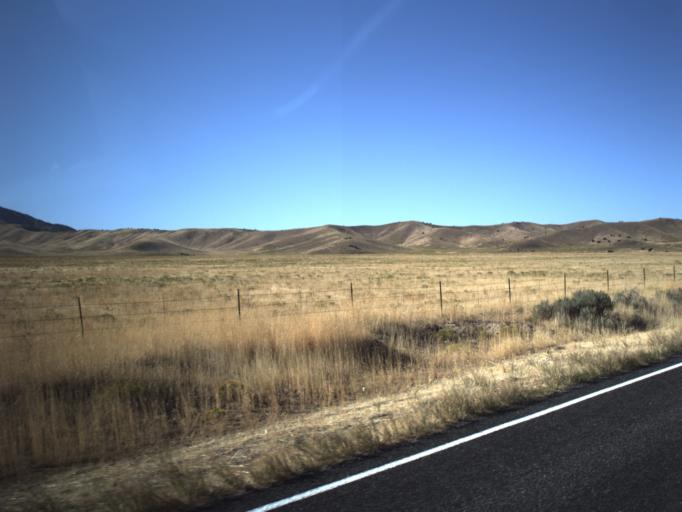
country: US
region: Utah
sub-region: Millard County
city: Delta
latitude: 39.4653
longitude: -112.2815
